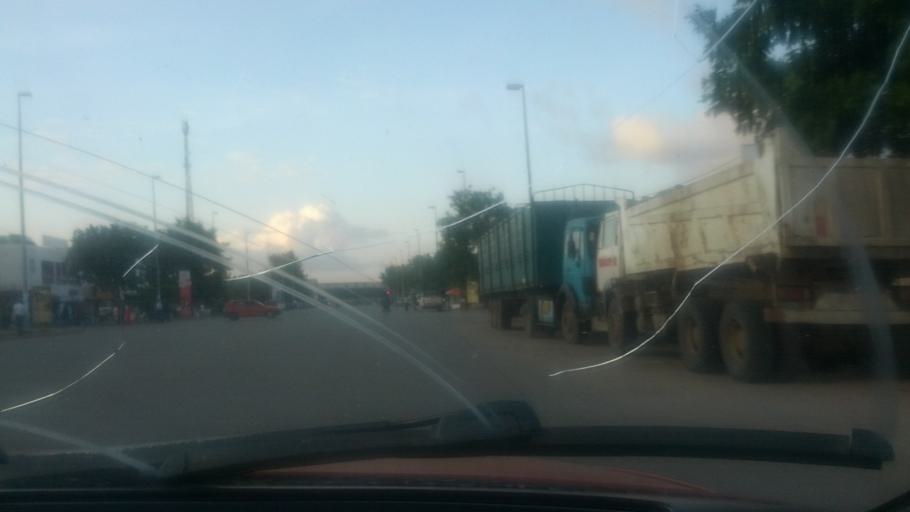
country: CI
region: Vallee du Bandama
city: Bouake
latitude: 7.6816
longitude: -5.0303
